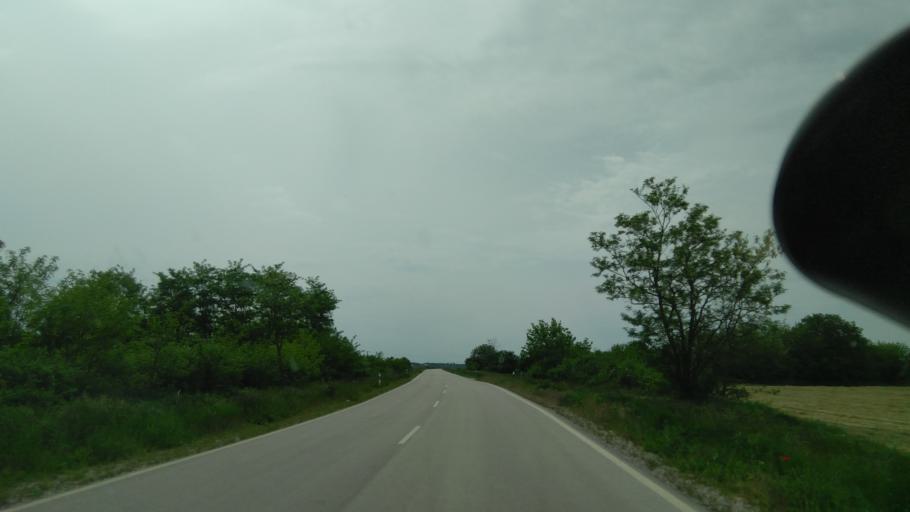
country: HU
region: Bekes
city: Mehkerek
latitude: 46.8675
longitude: 21.4967
